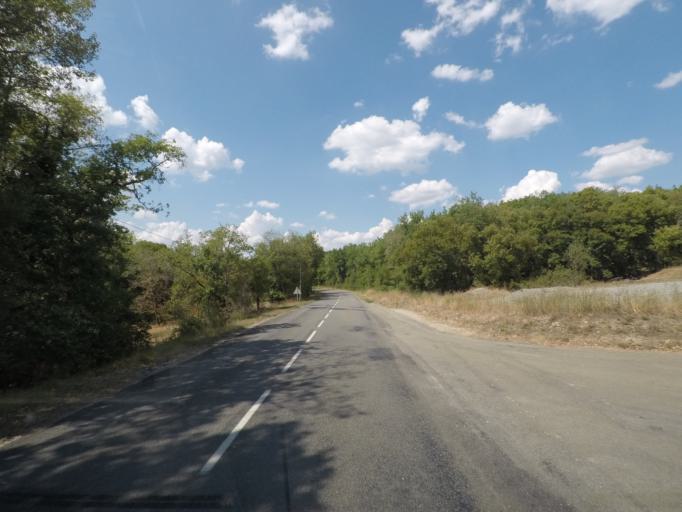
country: FR
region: Midi-Pyrenees
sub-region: Departement du Lot
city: Cahors
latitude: 44.5506
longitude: 1.5922
